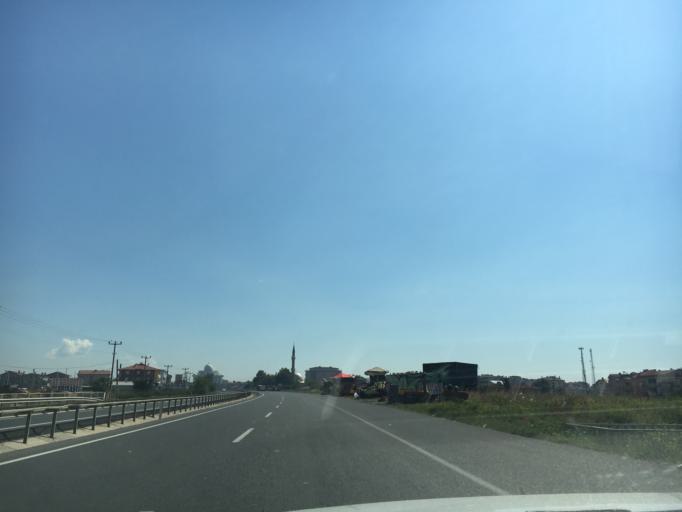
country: TR
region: Tekirdag
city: Marmara Ereglisi
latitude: 40.9729
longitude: 27.9425
